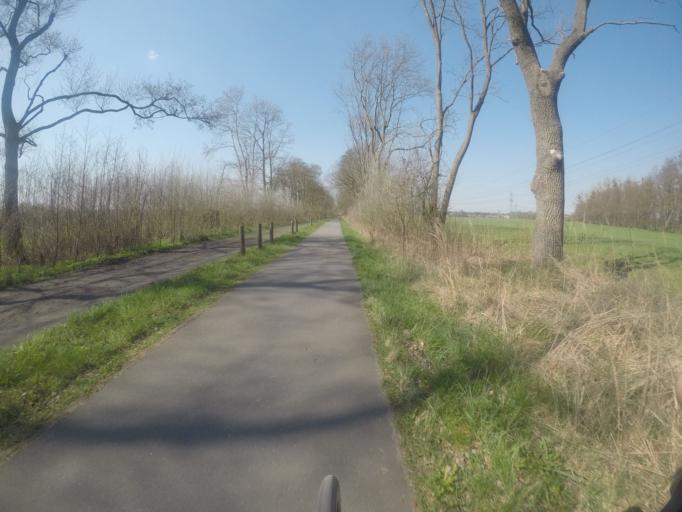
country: DE
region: Brandenburg
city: Falkensee
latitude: 52.6297
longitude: 13.0963
